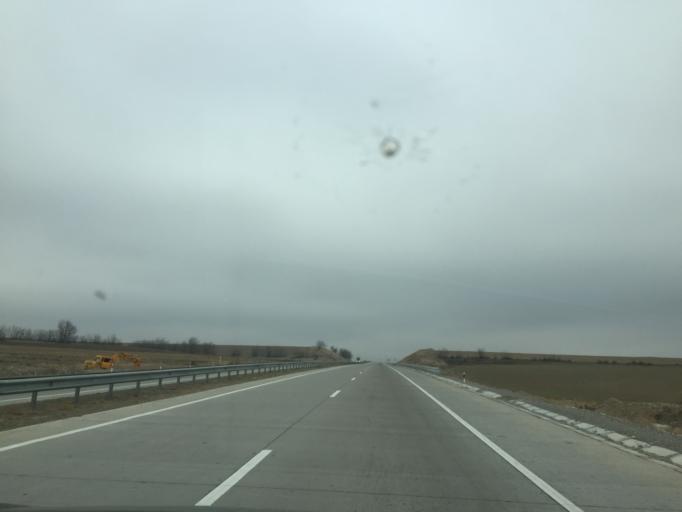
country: KZ
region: Ongtustik Qazaqstan
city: Aksu
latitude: 42.4756
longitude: 69.8897
